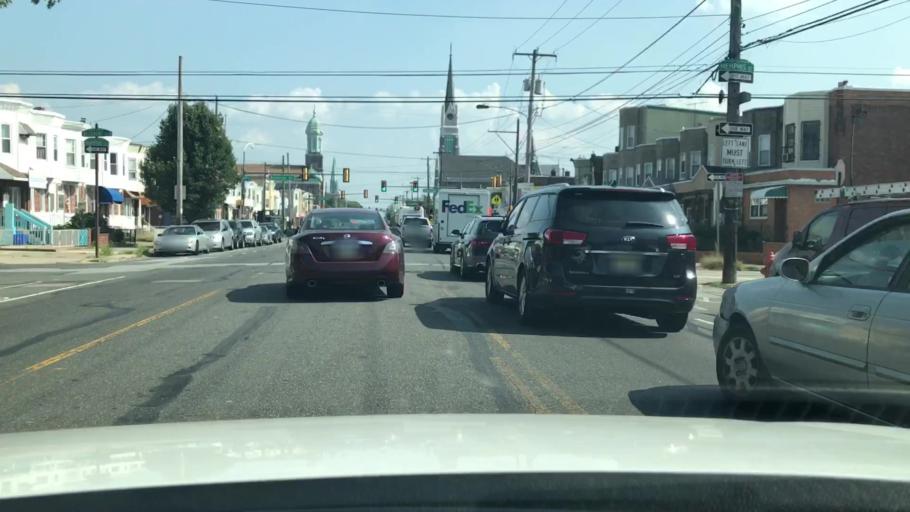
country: US
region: New Jersey
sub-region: Camden County
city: Merchantville
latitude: 39.9892
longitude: -75.1070
